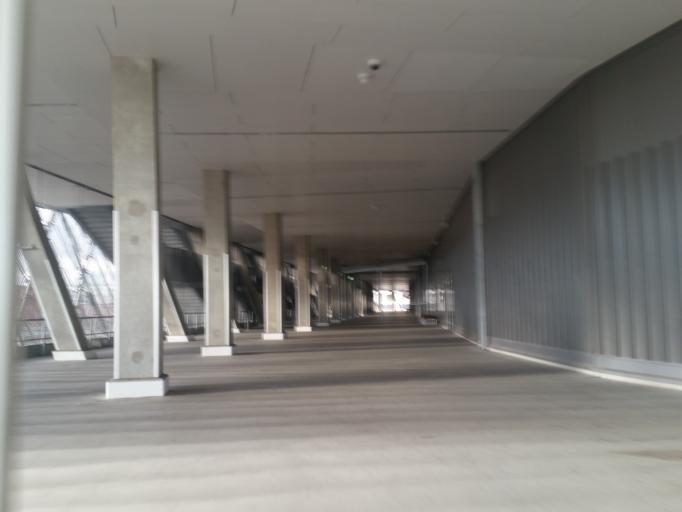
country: SE
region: Stockholm
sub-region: Stockholms Kommun
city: Arsta
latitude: 59.2901
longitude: 18.0838
